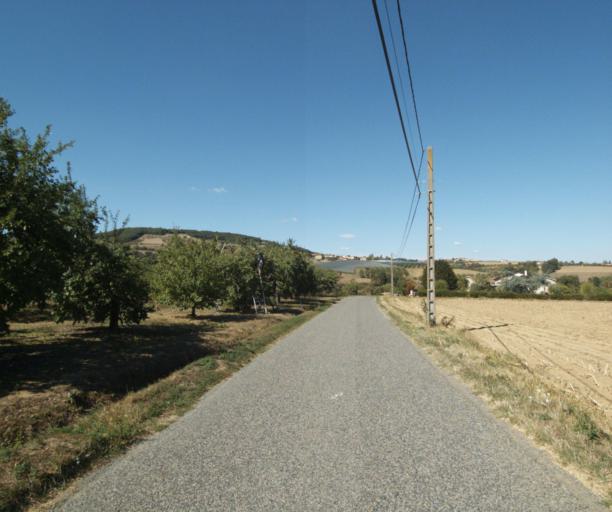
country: FR
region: Rhone-Alpes
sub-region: Departement du Rhone
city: Bessenay
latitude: 45.7849
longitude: 4.5493
